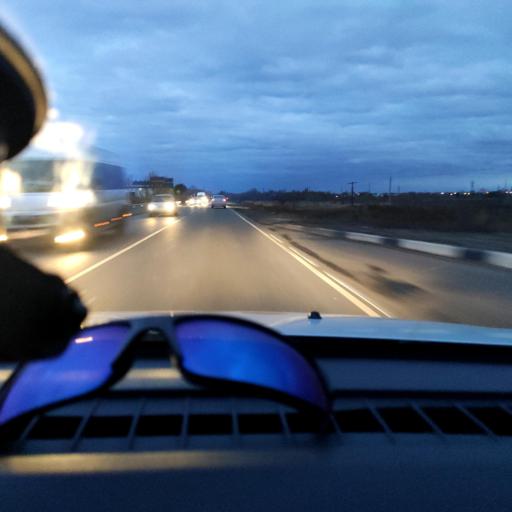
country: RU
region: Samara
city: Samara
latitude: 53.1225
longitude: 50.1172
